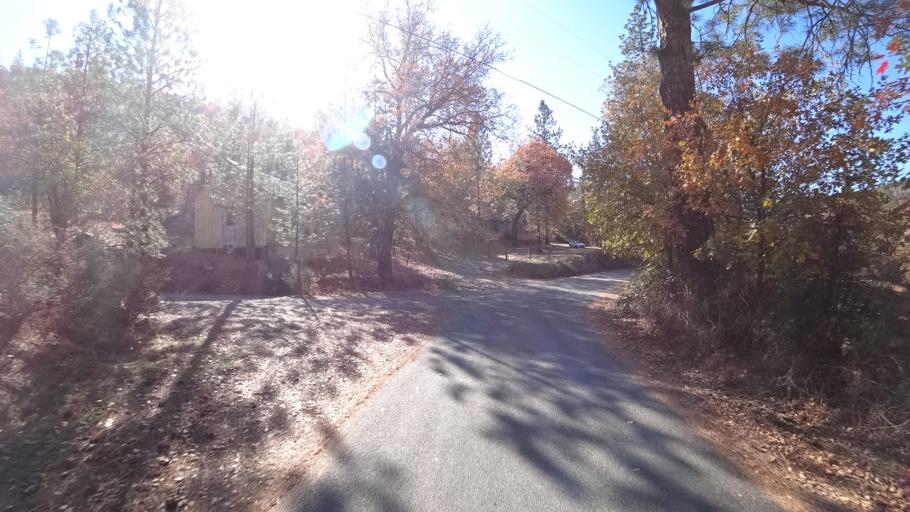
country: US
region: California
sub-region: Siskiyou County
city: Yreka
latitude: 41.8331
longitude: -122.8412
